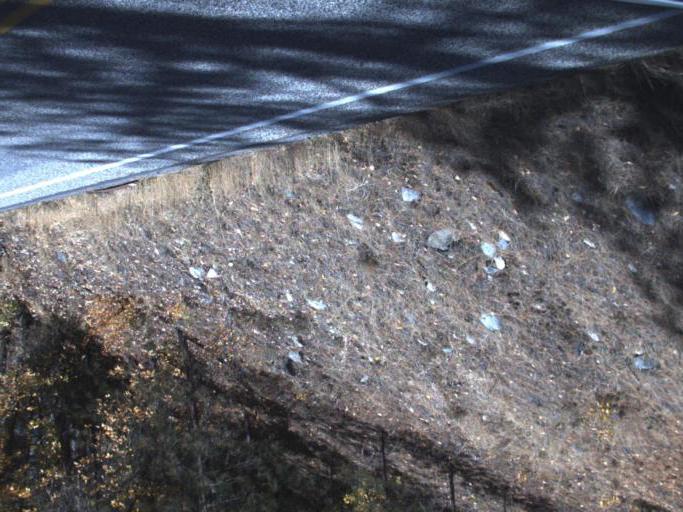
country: US
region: Washington
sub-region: Stevens County
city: Kettle Falls
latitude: 48.5922
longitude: -118.1653
